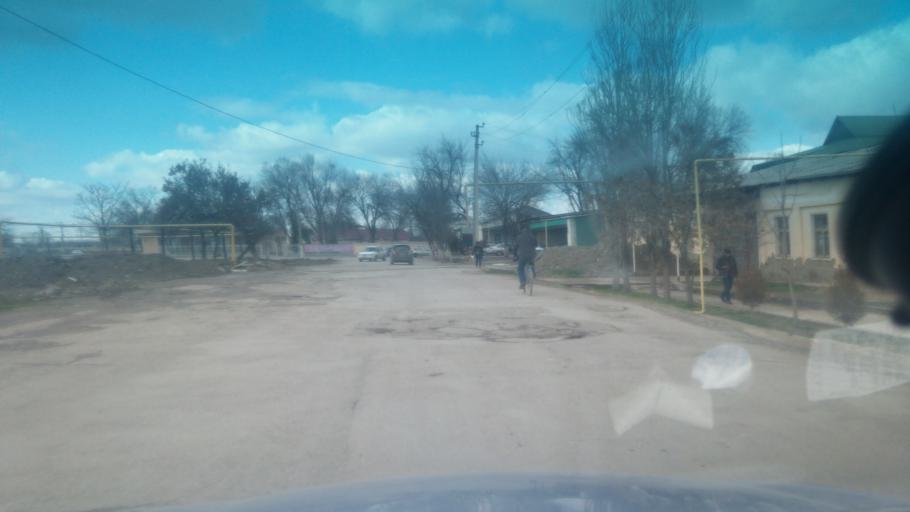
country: UZ
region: Sirdaryo
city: Guliston
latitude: 40.4986
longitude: 68.7653
